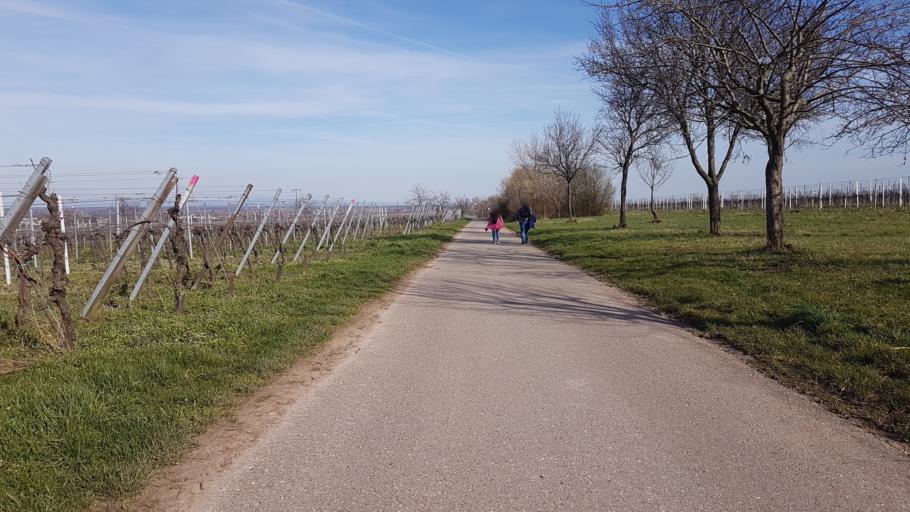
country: DE
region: Rheinland-Pfalz
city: Maikammer
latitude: 49.2959
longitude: 8.1243
